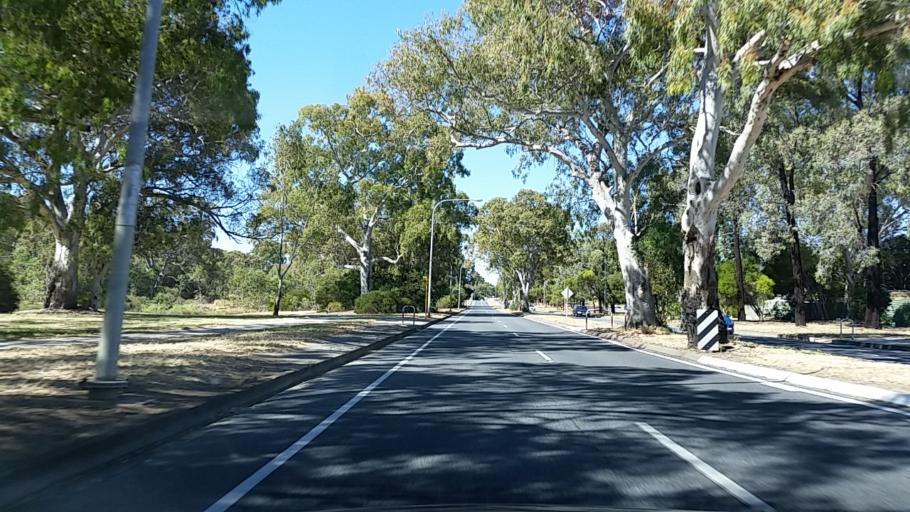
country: AU
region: South Australia
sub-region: Tea Tree Gully
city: Hope Valley
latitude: -34.8125
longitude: 138.6949
